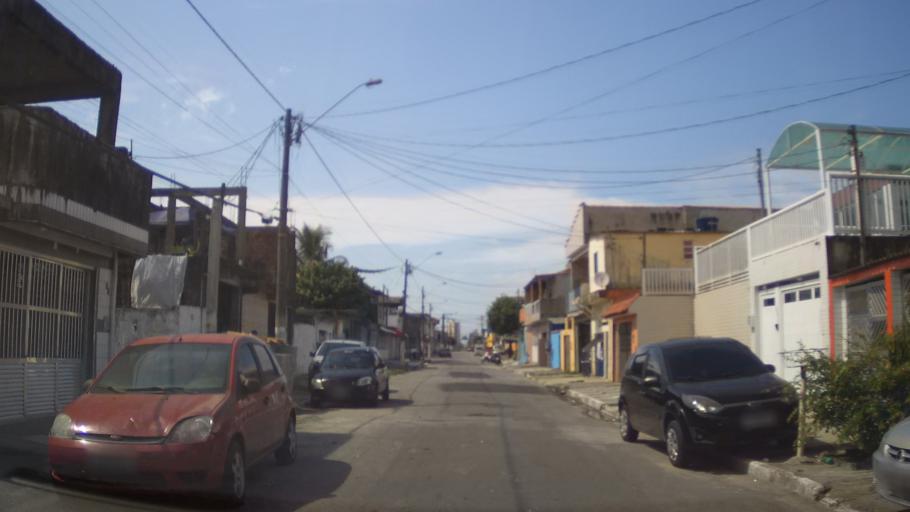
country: BR
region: Sao Paulo
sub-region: Praia Grande
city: Praia Grande
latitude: -24.0183
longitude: -46.4847
